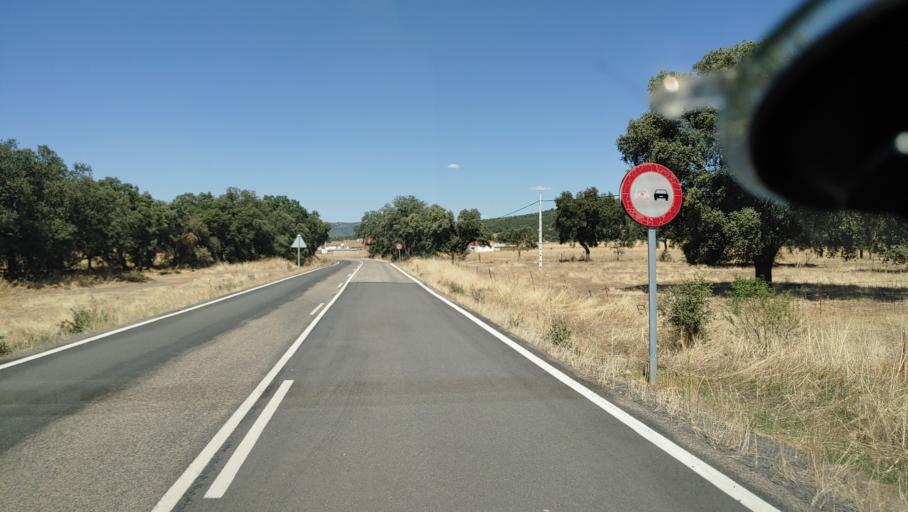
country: ES
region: Castille-La Mancha
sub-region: Provincia de Ciudad Real
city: Almaden
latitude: 38.8050
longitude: -4.7058
